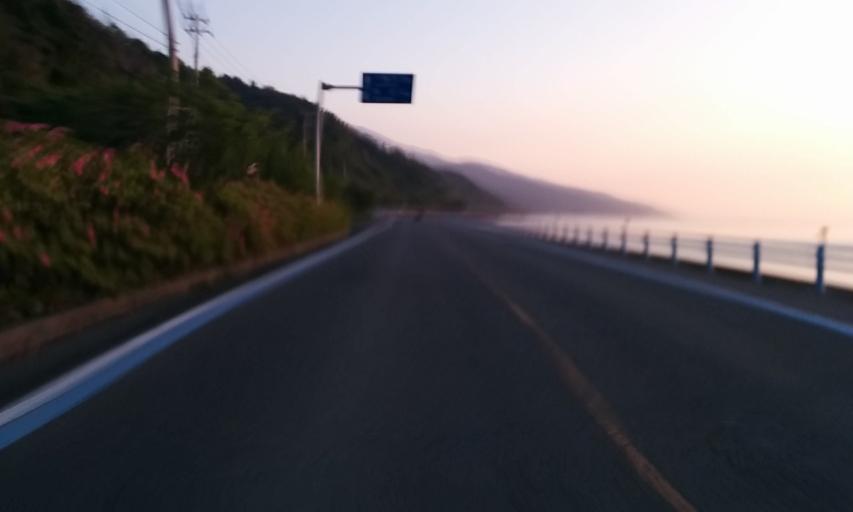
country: JP
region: Ehime
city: Iyo
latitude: 33.6682
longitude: 132.6087
